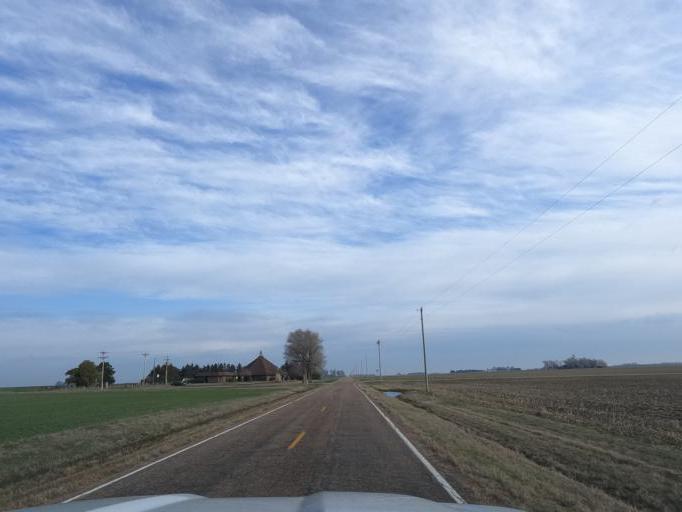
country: US
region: Kansas
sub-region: Rice County
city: Sterling
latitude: 38.0853
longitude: -98.2521
